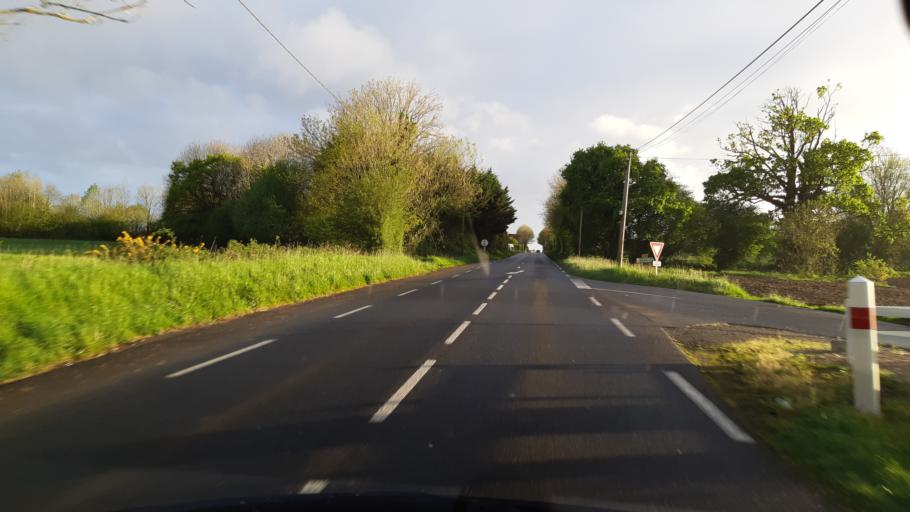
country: FR
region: Lower Normandy
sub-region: Departement de la Manche
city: Tessy-sur-Vire
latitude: 49.0223
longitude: -1.1464
